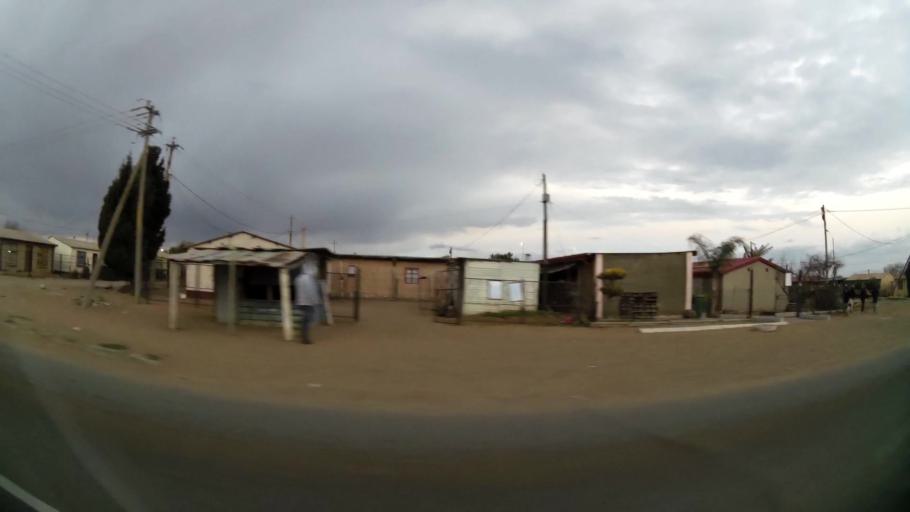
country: ZA
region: Orange Free State
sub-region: Lejweleputswa District Municipality
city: Welkom
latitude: -27.9712
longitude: 26.7858
